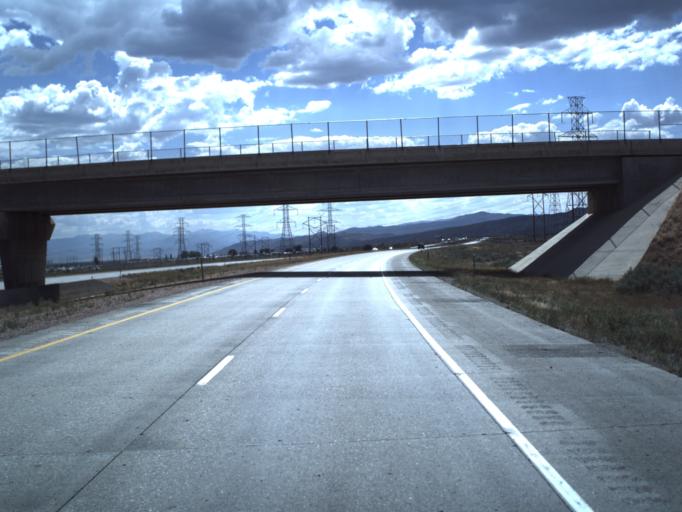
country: US
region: Utah
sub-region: Sevier County
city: Aurora
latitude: 38.8608
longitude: -111.9841
